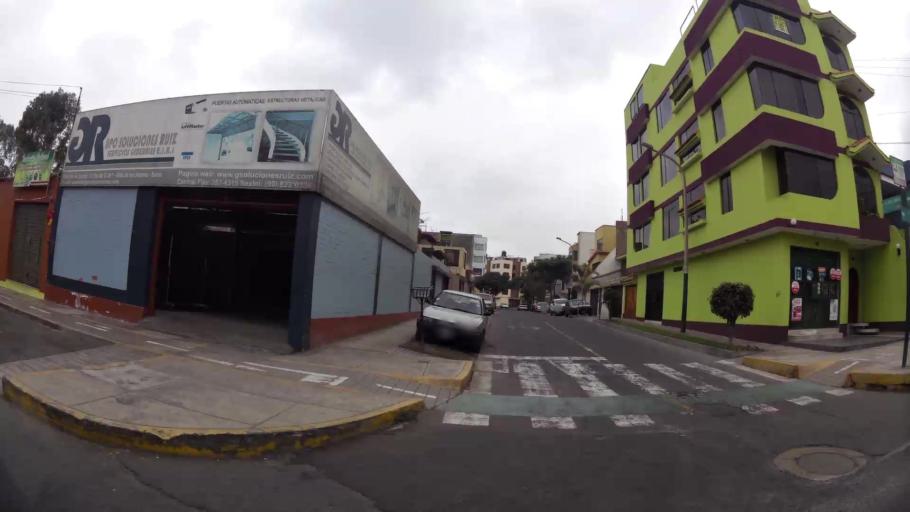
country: PE
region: Lima
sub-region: Lima
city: Surco
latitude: -12.1671
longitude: -76.9907
